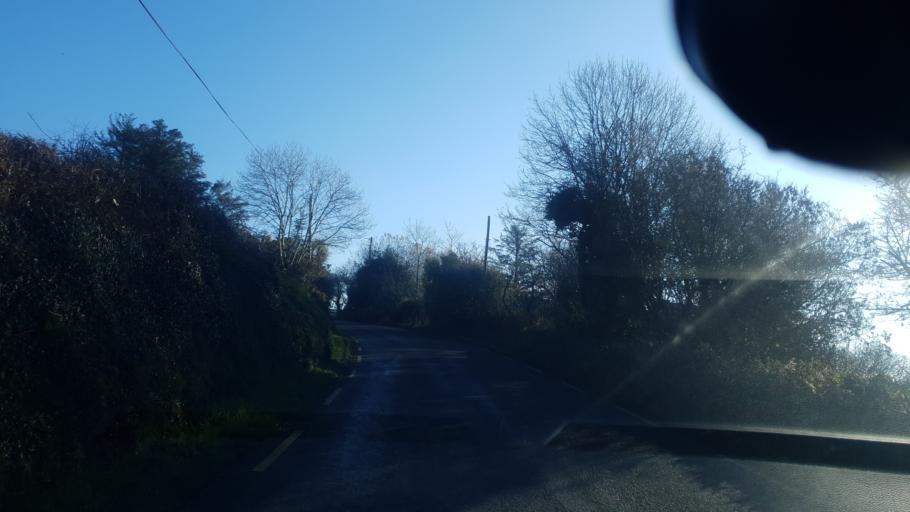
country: IE
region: Munster
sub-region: Ciarrai
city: Cill Airne
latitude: 52.1085
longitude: -9.4942
